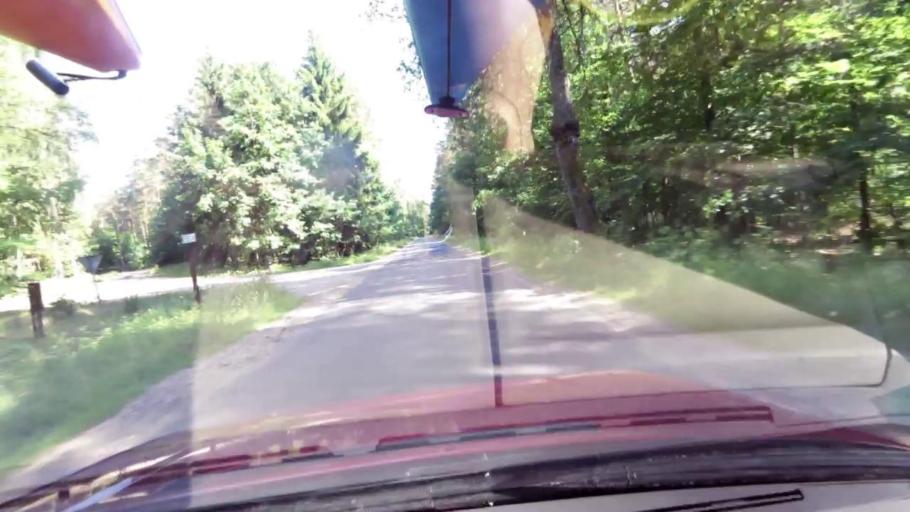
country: PL
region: Pomeranian Voivodeship
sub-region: Powiat slupski
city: Kepice
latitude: 54.1364
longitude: 16.9286
